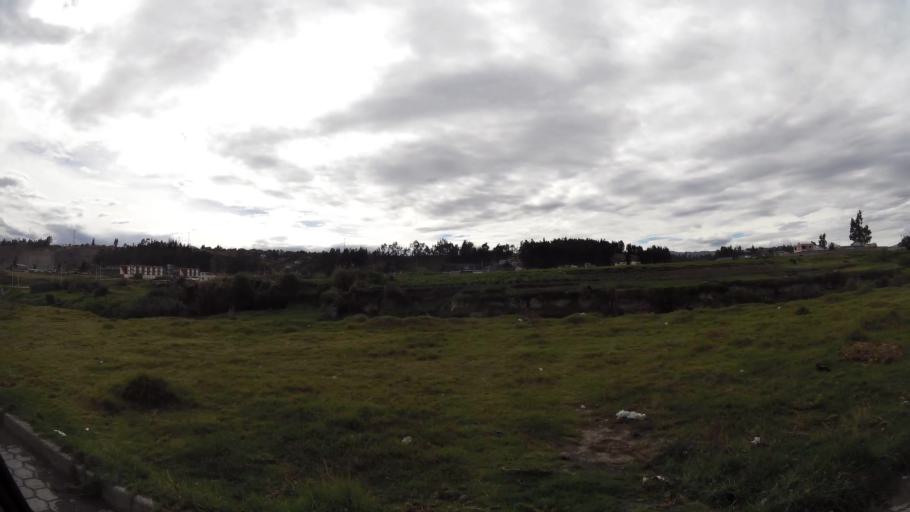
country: EC
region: Cotopaxi
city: Latacunga
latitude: -0.9492
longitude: -78.6174
